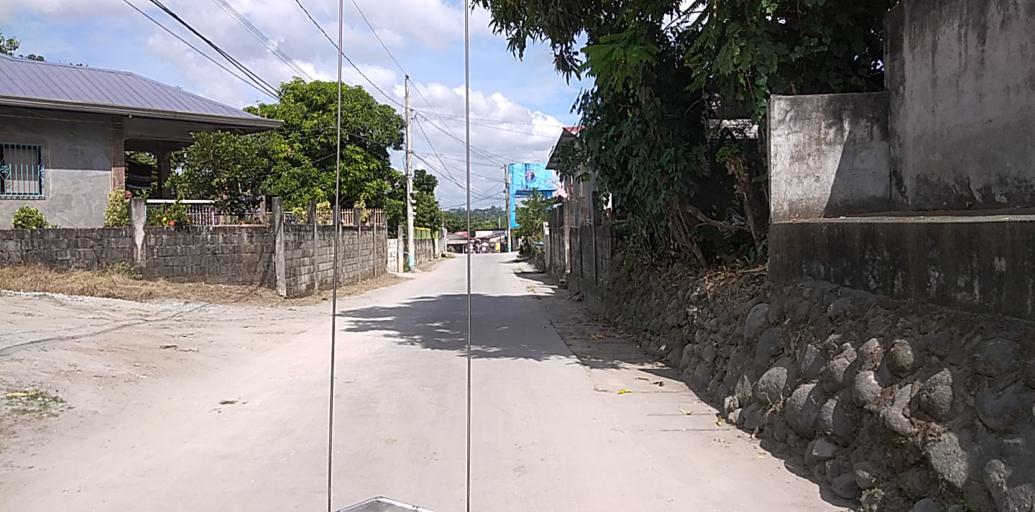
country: PH
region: Central Luzon
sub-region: Province of Pampanga
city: Porac
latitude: 15.0639
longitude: 120.5361
